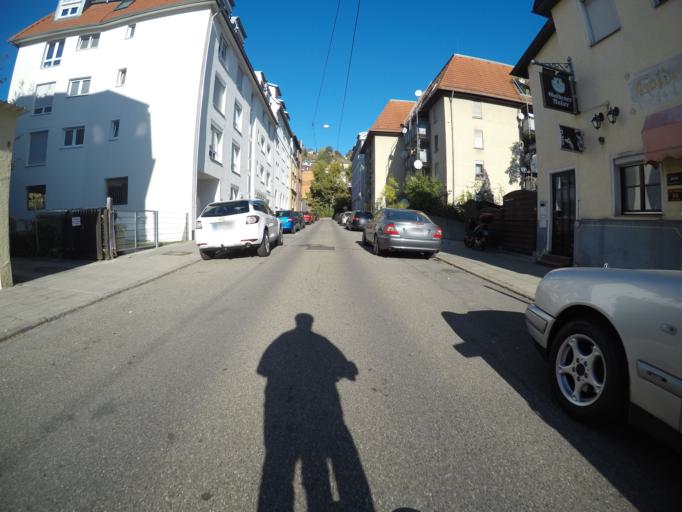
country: DE
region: Baden-Wuerttemberg
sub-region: Regierungsbezirk Stuttgart
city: Stuttgart
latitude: 48.7610
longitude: 9.1561
